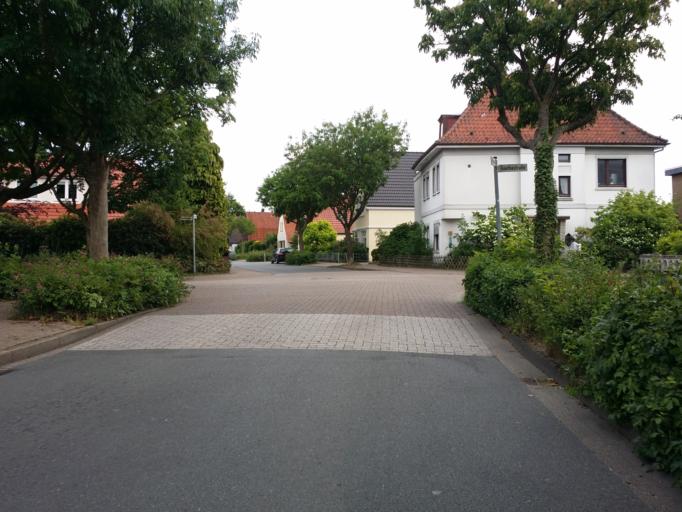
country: DE
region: Lower Saxony
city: Oldenburg
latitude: 53.1561
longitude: 8.2252
